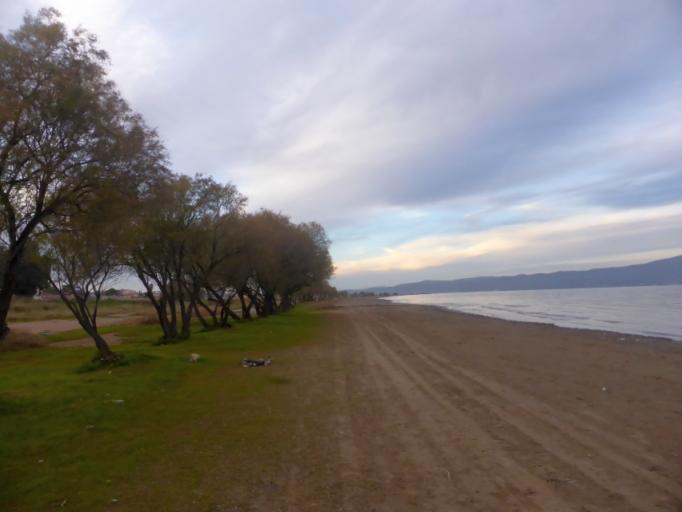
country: GR
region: Attica
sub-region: Nomarchia Anatolikis Attikis
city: Skala Oropou
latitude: 38.3241
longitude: 23.7820
